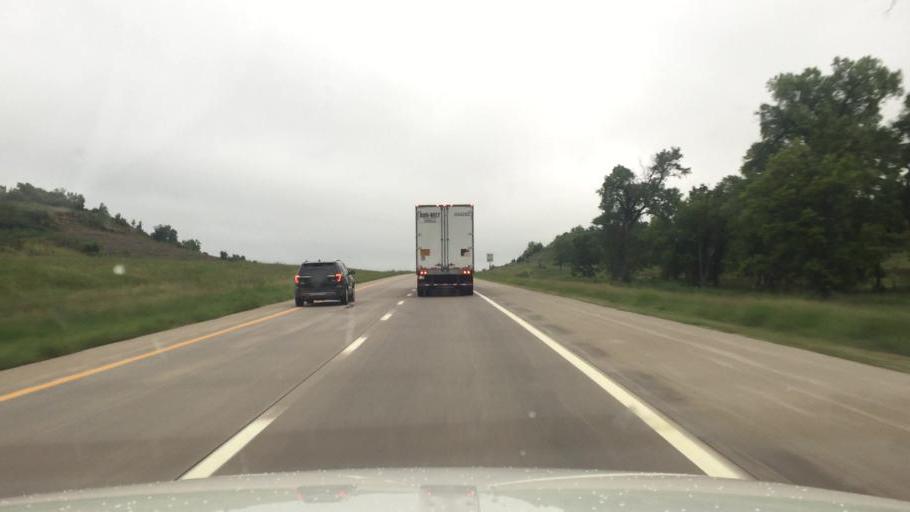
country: US
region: Kansas
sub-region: Montgomery County
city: Cherryvale
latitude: 37.2176
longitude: -95.5856
